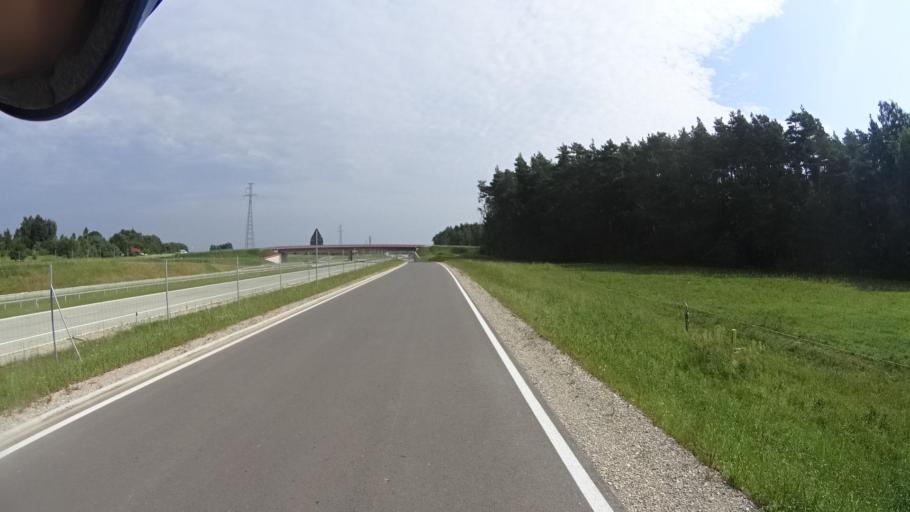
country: PL
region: Masovian Voivodeship
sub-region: Powiat piaseczynski
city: Tarczyn
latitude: 51.9643
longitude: 20.8581
